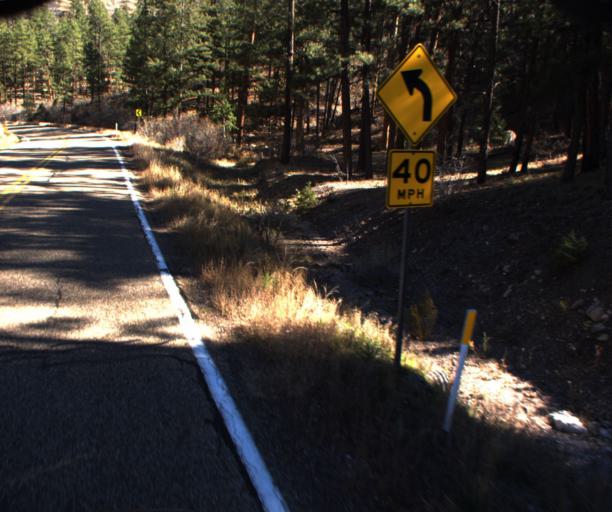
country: US
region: Arizona
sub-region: Coconino County
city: Fredonia
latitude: 36.7333
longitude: -112.1330
